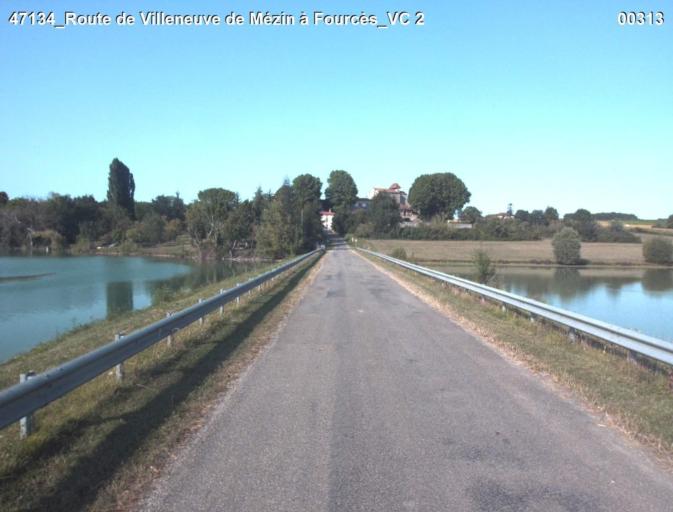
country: FR
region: Aquitaine
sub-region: Departement du Lot-et-Garonne
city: Mezin
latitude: 44.0146
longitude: 0.2457
